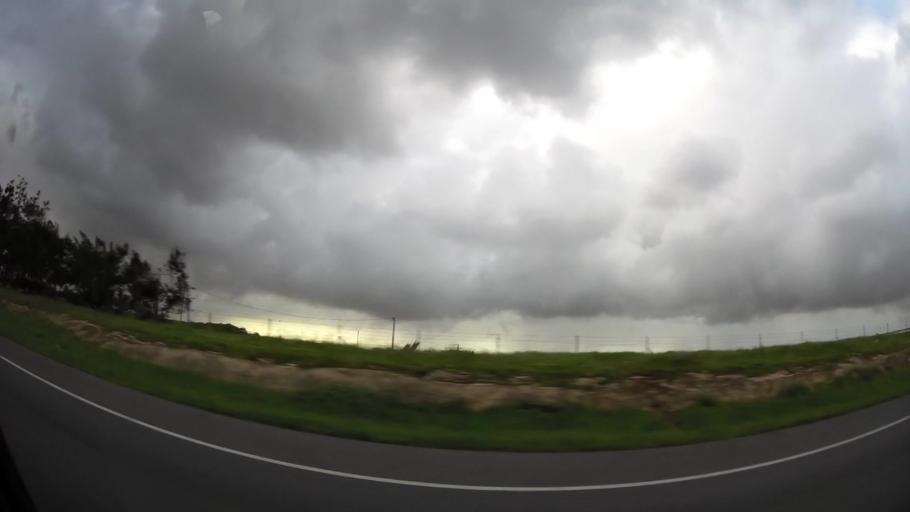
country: MA
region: Grand Casablanca
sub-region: Mediouna
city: Tit Mellil
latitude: 33.5967
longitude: -7.4430
